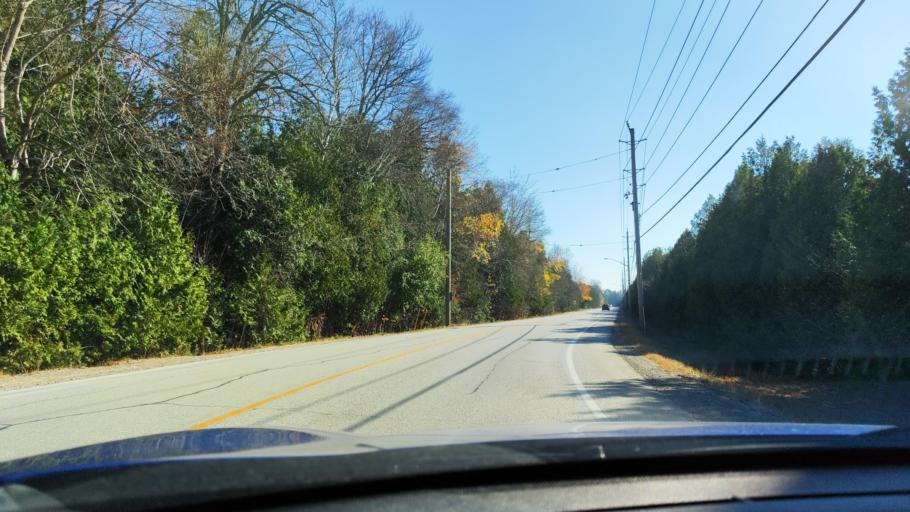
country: CA
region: Ontario
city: Wasaga Beach
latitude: 44.5060
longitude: -79.9929
